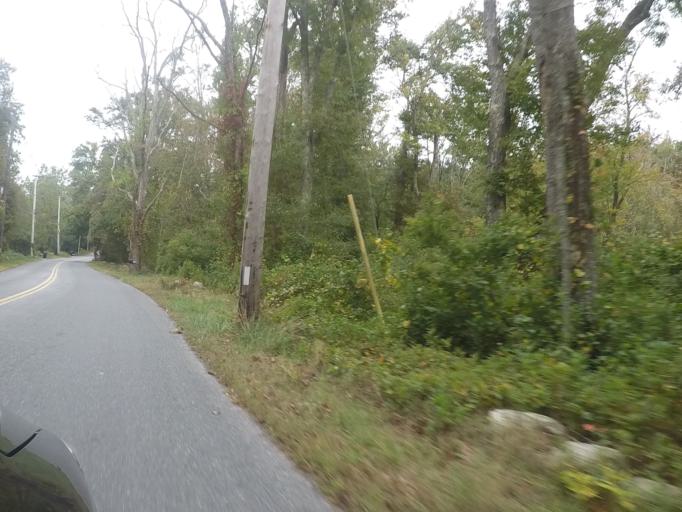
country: US
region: Massachusetts
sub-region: Bristol County
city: Smith Mills
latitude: 41.5652
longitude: -71.0067
